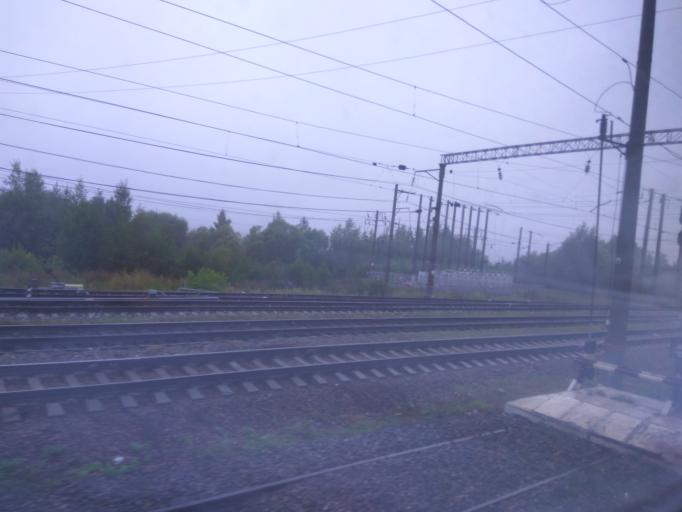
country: RU
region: Moskovskaya
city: Uzunovo
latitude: 54.5512
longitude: 38.6199
